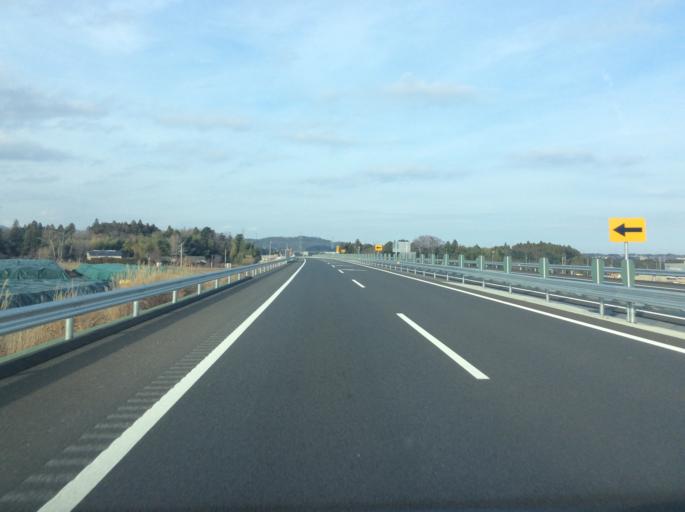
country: JP
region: Fukushima
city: Namie
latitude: 37.3813
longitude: 140.9665
